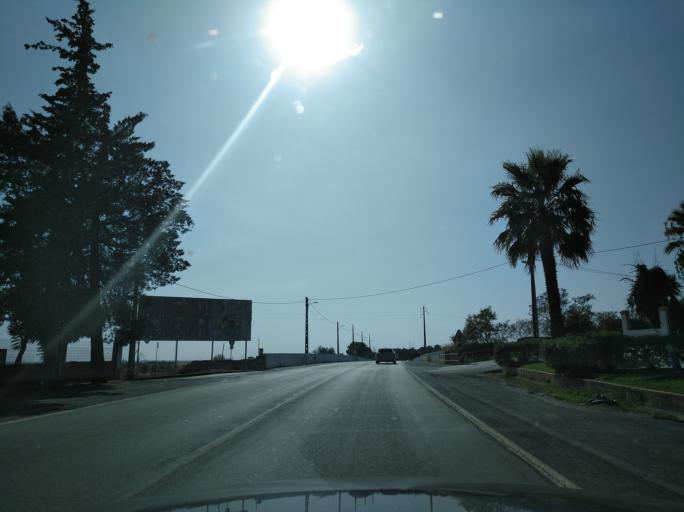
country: ES
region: Andalusia
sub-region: Provincia de Huelva
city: Rosal de la Frontera
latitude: 37.9497
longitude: -7.3001
